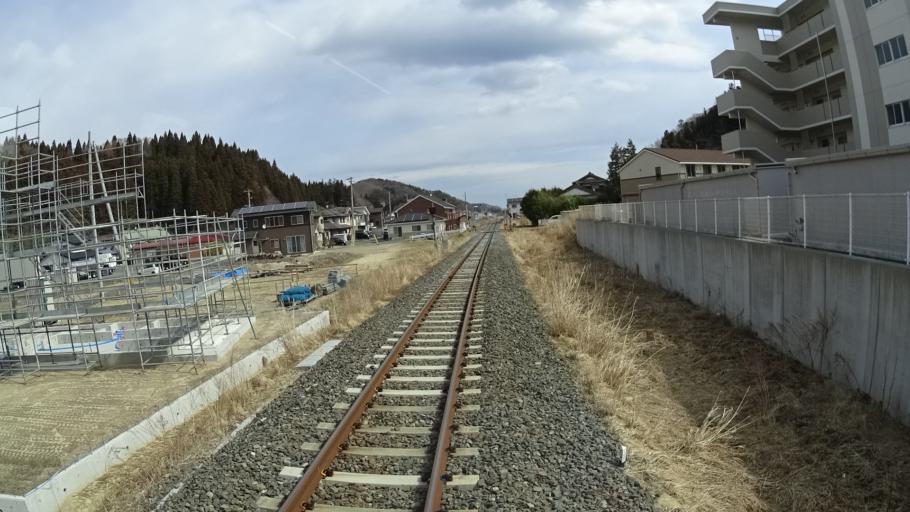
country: JP
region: Iwate
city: Miyako
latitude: 39.6155
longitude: 141.9403
